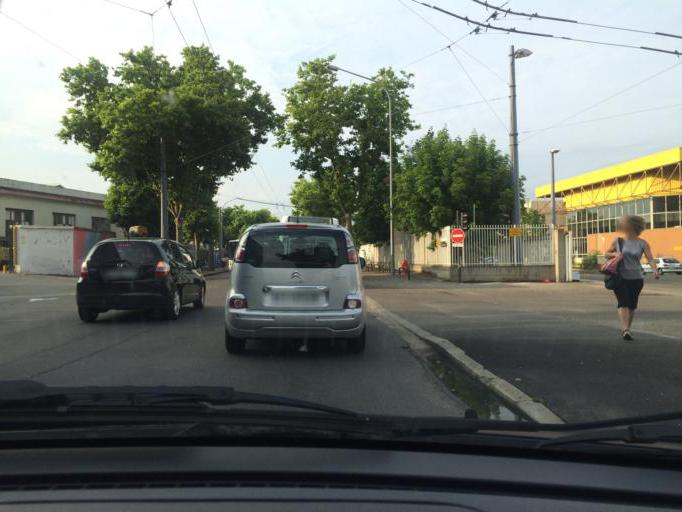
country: FR
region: Rhone-Alpes
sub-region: Departement du Rhone
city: Vaulx-en-Velin
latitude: 45.7602
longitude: 4.9207
